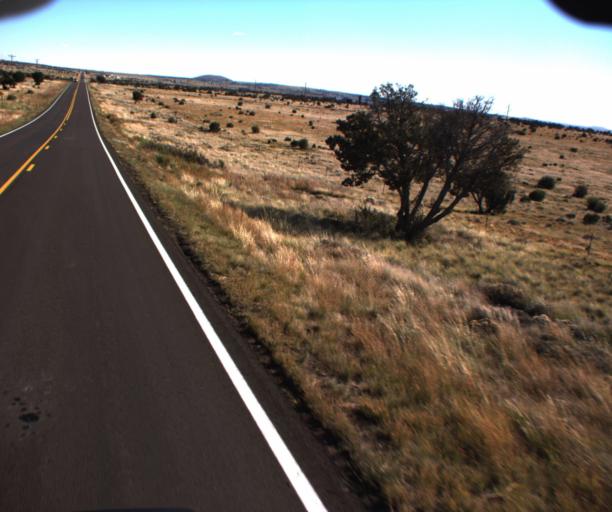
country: US
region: Arizona
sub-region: Navajo County
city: White Mountain Lake
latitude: 34.3760
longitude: -109.6875
